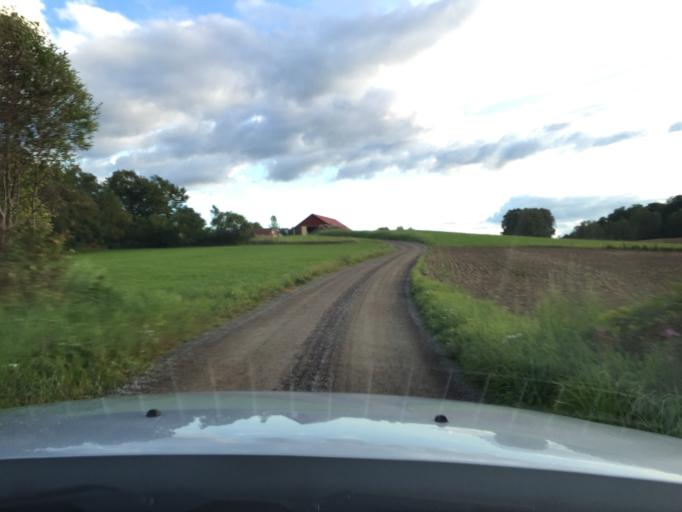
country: SE
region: Skane
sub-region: Hassleholms Kommun
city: Sosdala
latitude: 56.0395
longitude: 13.7100
